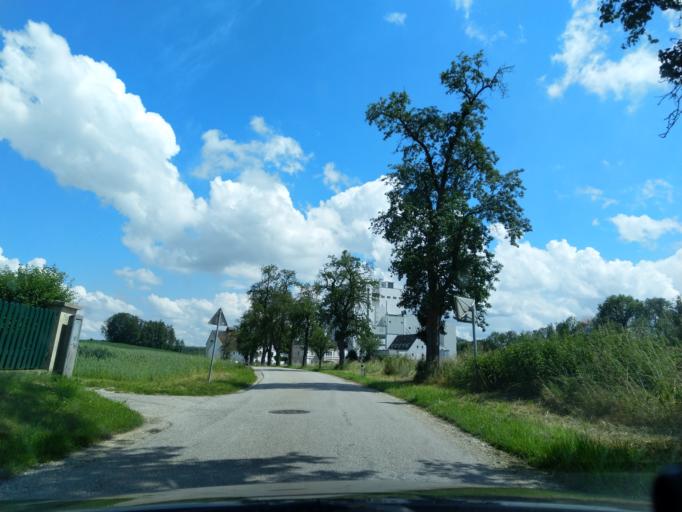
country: DE
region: Bavaria
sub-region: Lower Bavaria
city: Bad Fussing
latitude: 48.3208
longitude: 13.3401
